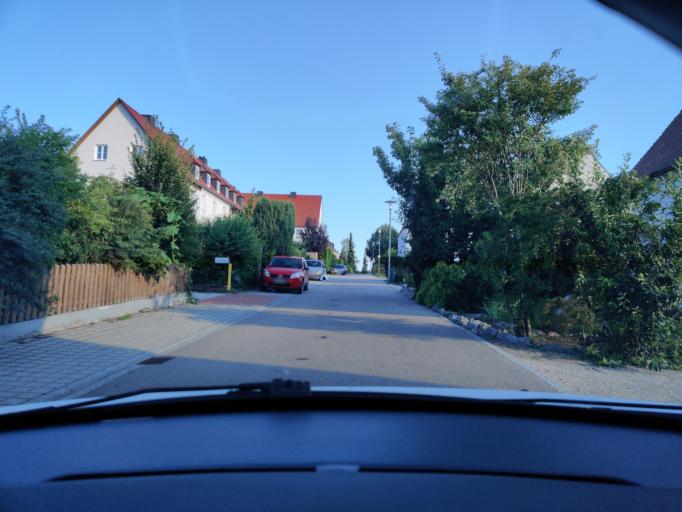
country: DE
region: Bavaria
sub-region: Upper Palatinate
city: Stulln
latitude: 49.4234
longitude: 12.1484
